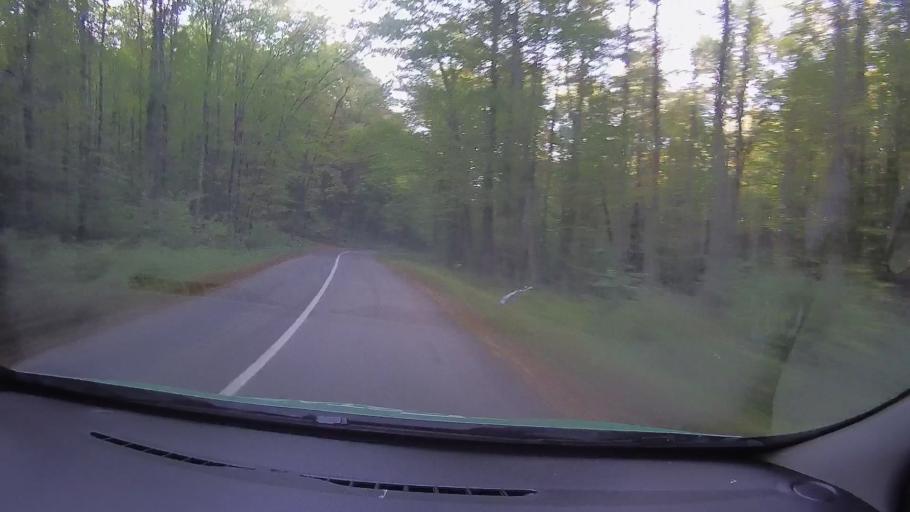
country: RO
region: Timis
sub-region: Comuna Nadrag
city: Nadrag
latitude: 45.6803
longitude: 22.1574
